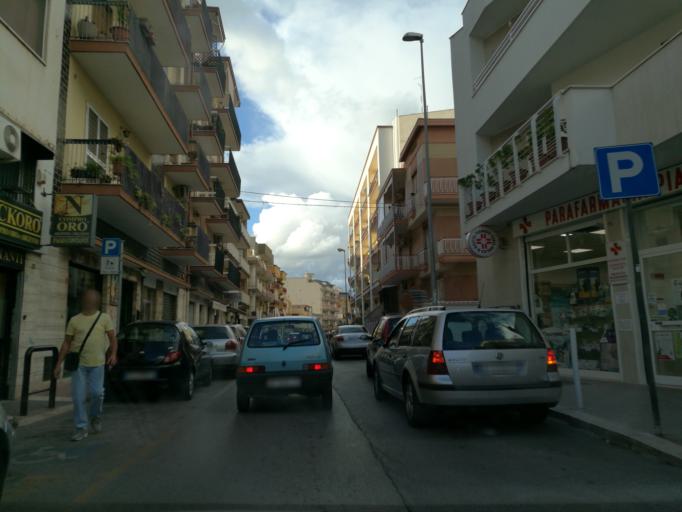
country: IT
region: Apulia
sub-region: Provincia di Bari
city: Valenzano
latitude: 41.0446
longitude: 16.8859
